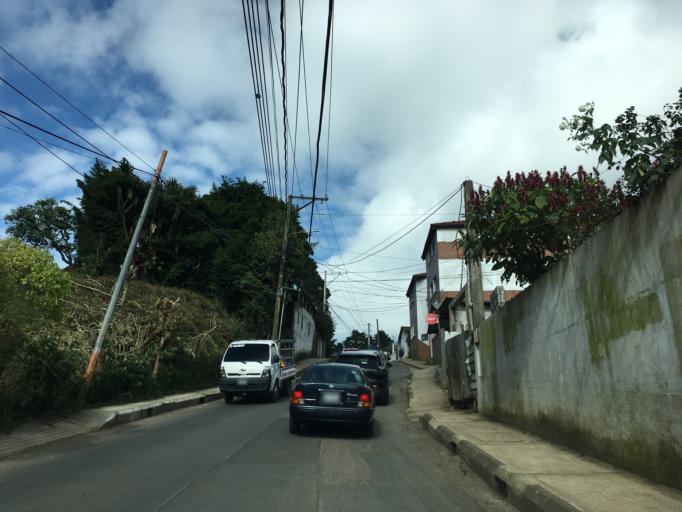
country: GT
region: Guatemala
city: San Jose Pinula
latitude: 14.5627
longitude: -90.4371
